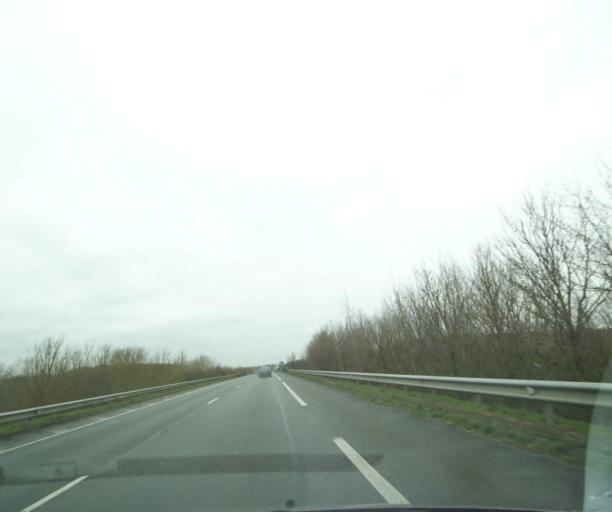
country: FR
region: Picardie
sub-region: Departement de l'Oise
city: Noyon
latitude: 49.5681
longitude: 2.9893
